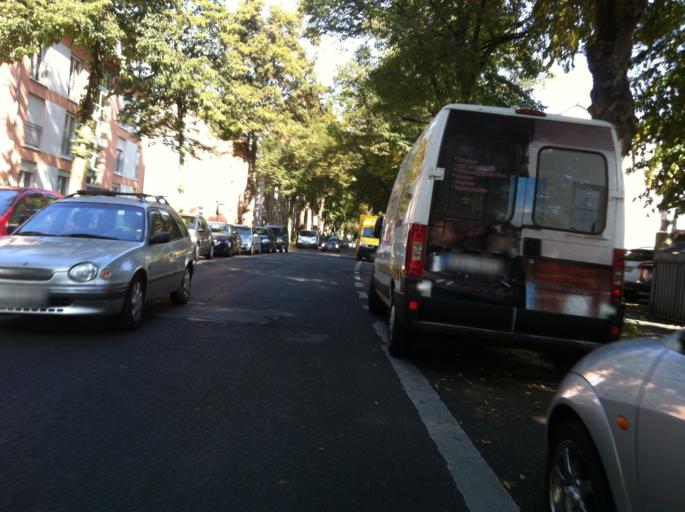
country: DE
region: North Rhine-Westphalia
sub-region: Regierungsbezirk Koln
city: Kalk
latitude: 50.9276
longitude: 7.0216
